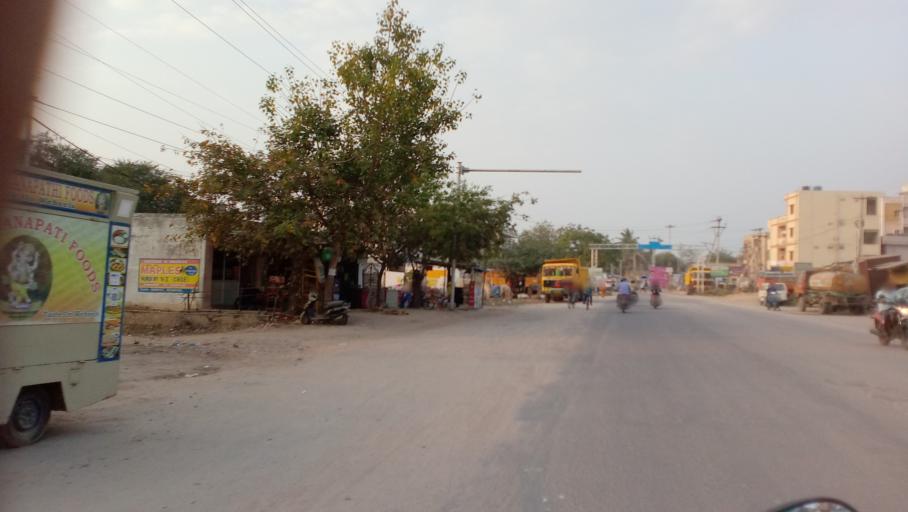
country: IN
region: Telangana
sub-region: Medak
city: Serilingampalle
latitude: 17.5078
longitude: 78.3184
